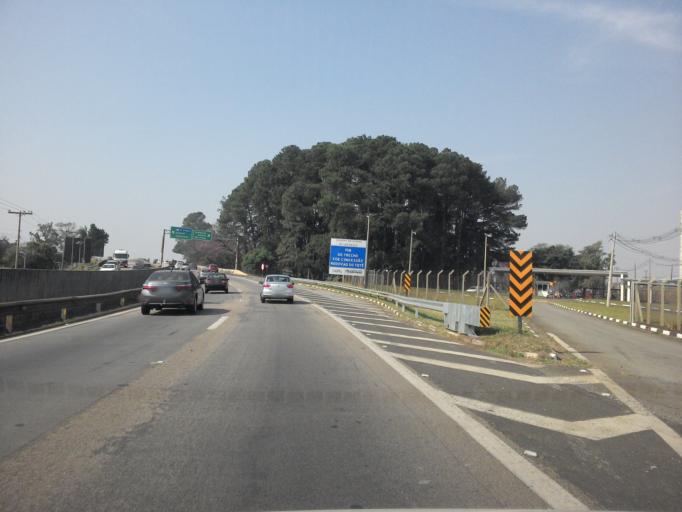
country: BR
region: Sao Paulo
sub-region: Campinas
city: Campinas
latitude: -22.8995
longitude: -47.1143
